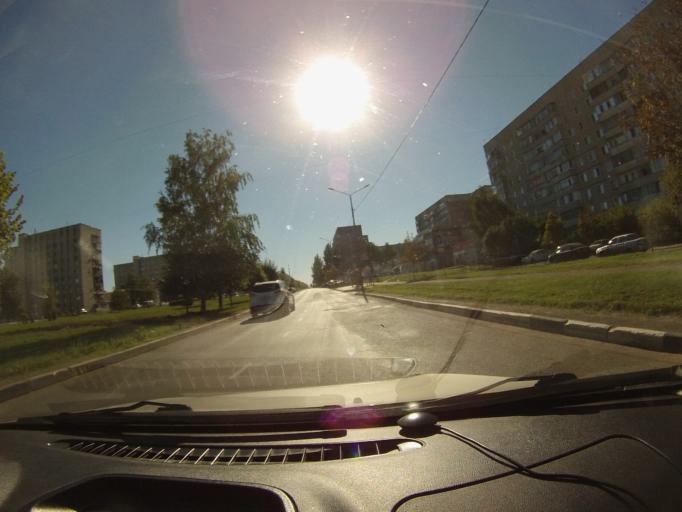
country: RU
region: Tambov
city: Tambov
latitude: 52.7665
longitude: 41.4134
